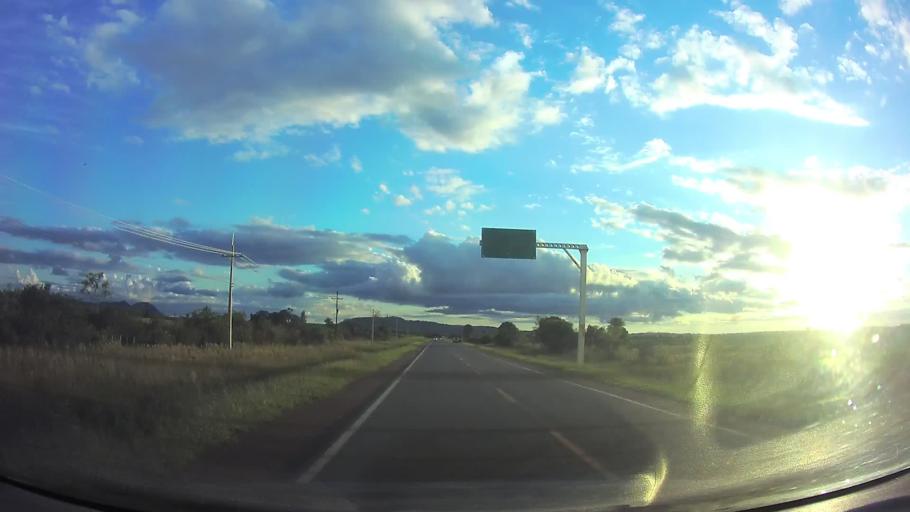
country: PY
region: Paraguari
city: Carapegua
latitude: -25.7425
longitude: -57.2128
